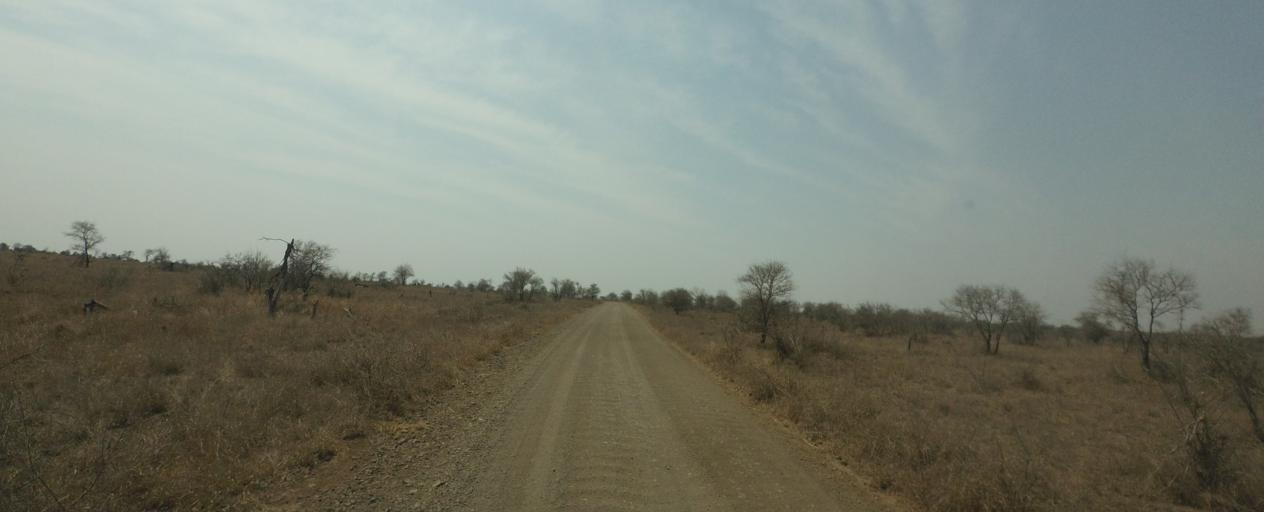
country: ZA
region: Limpopo
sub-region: Mopani District Municipality
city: Phalaborwa
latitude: -24.2601
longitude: 31.6675
